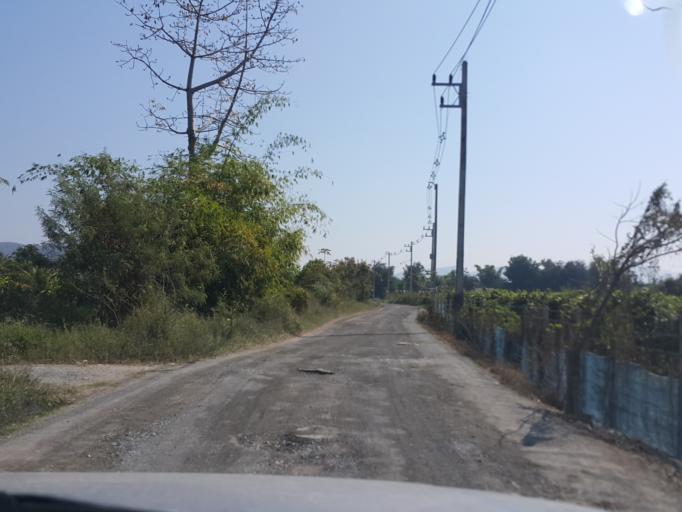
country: TH
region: Chiang Mai
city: San Kamphaeng
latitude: 18.8368
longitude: 99.1473
